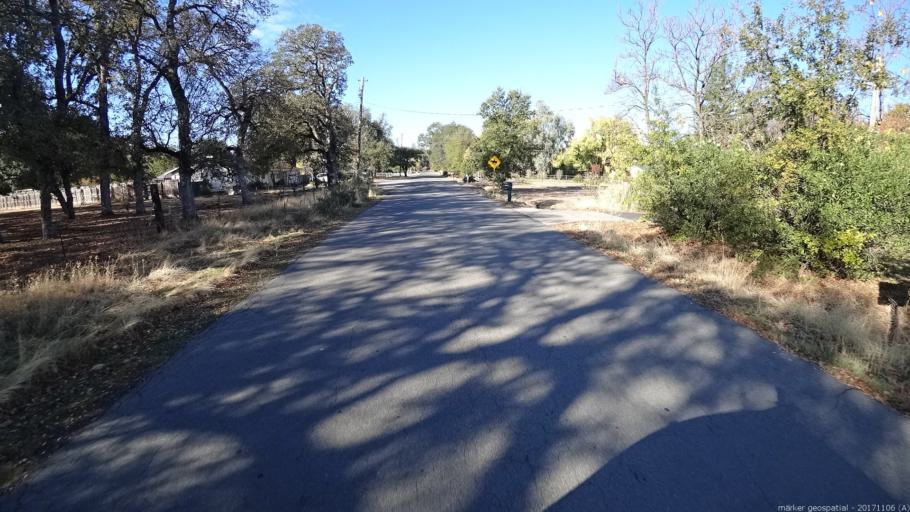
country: US
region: California
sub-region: Shasta County
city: Palo Cedro
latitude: 40.5493
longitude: -122.2392
